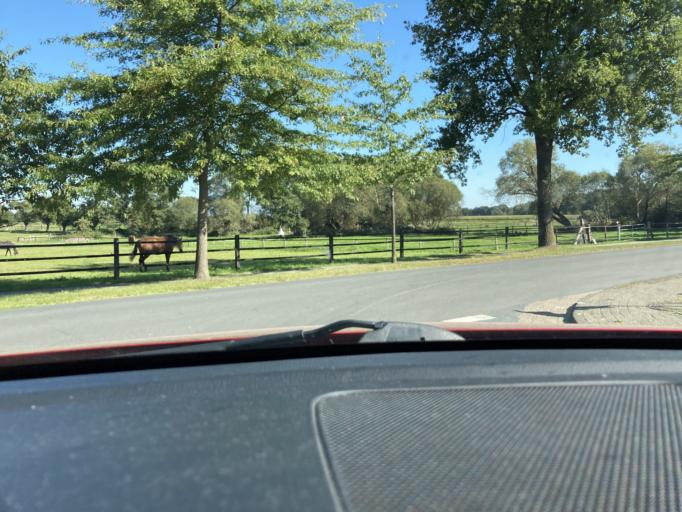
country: DE
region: Lower Saxony
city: Horstedt
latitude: 53.1779
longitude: 9.2345
